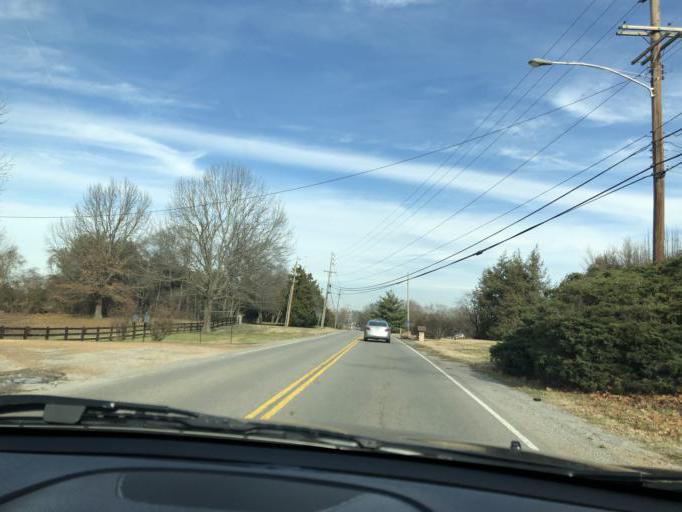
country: US
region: Tennessee
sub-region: Davidson County
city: Lakewood
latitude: 36.1890
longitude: -86.6747
